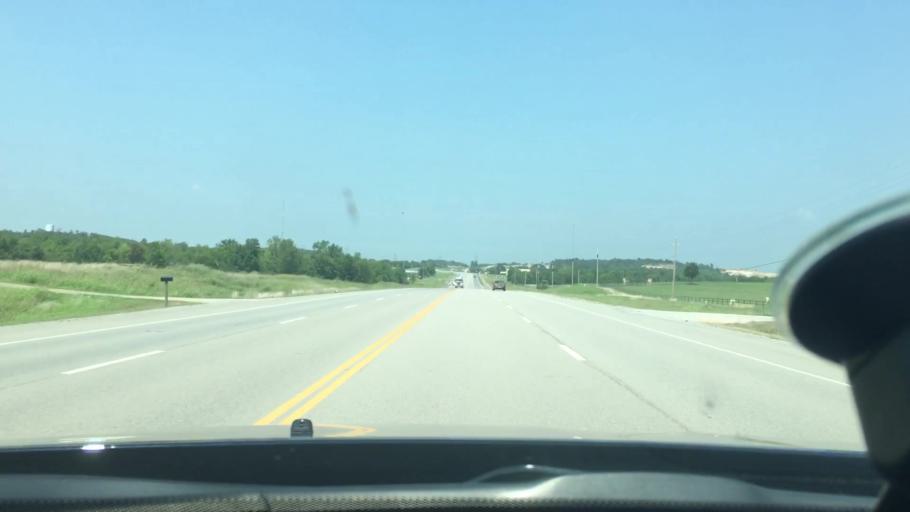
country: US
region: Oklahoma
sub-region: Atoka County
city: Atoka
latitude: 34.3624
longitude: -96.0977
